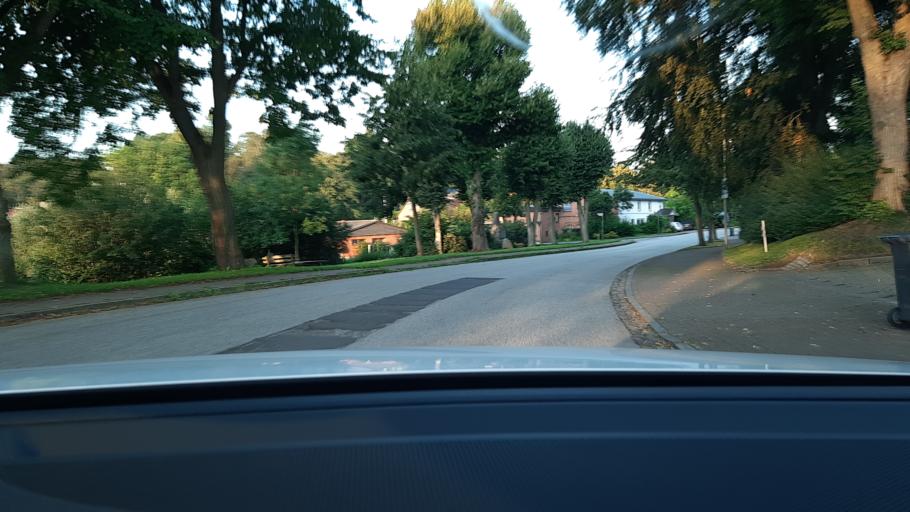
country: DE
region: Schleswig-Holstein
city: Westerau
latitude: 53.7791
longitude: 10.4924
